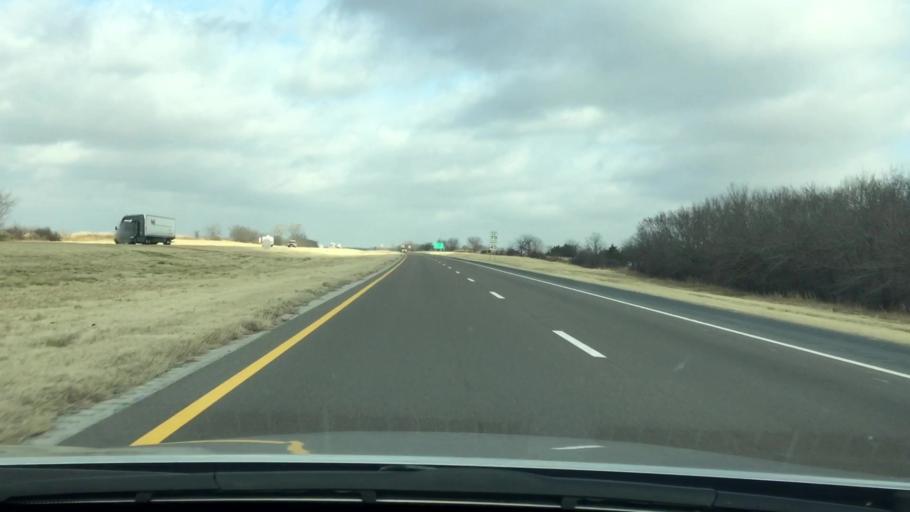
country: US
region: Oklahoma
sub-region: Garvin County
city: Maysville
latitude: 34.8352
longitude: -97.3126
